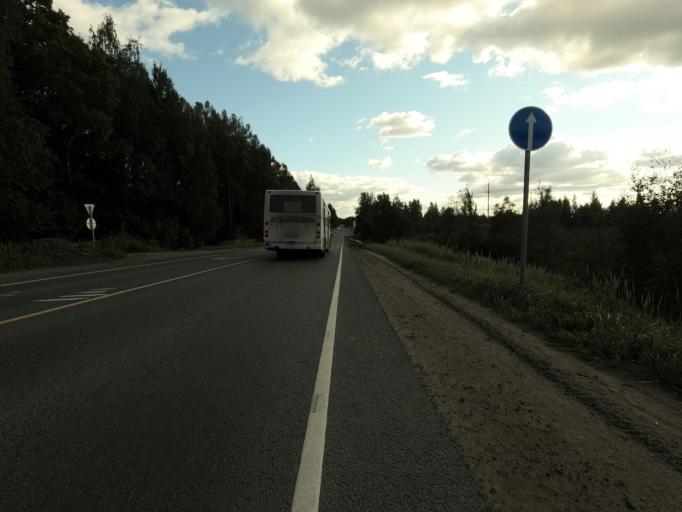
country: RU
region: Leningrad
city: Vsevolozhsk
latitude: 59.9797
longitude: 30.6540
